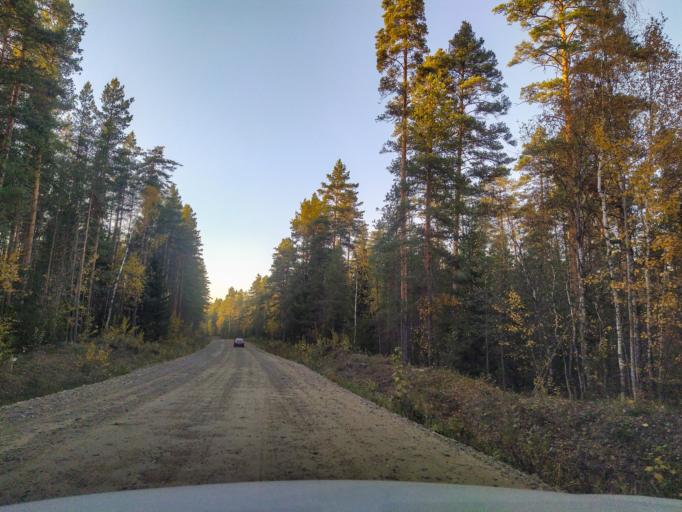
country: RU
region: Leningrad
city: Kuznechnoye
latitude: 61.3240
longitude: 29.9917
